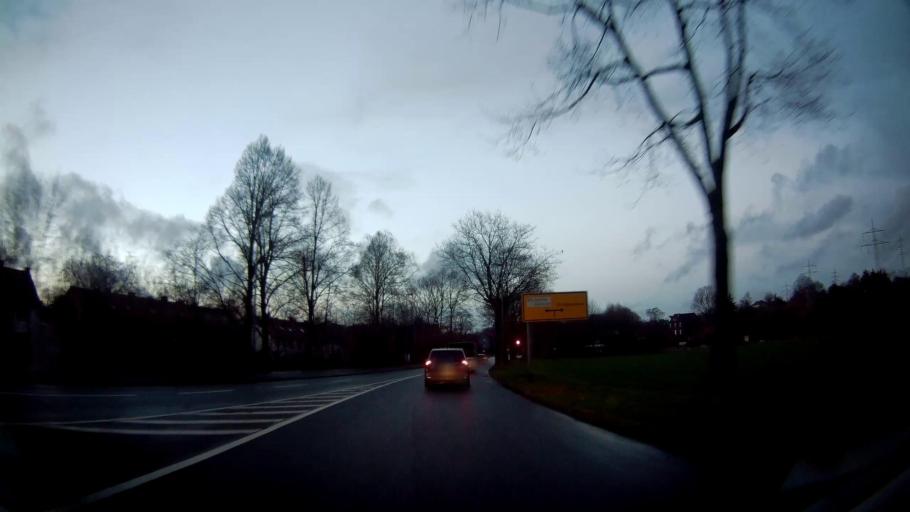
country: DE
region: North Rhine-Westphalia
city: Castrop-Rauxel
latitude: 51.4984
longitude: 7.2894
